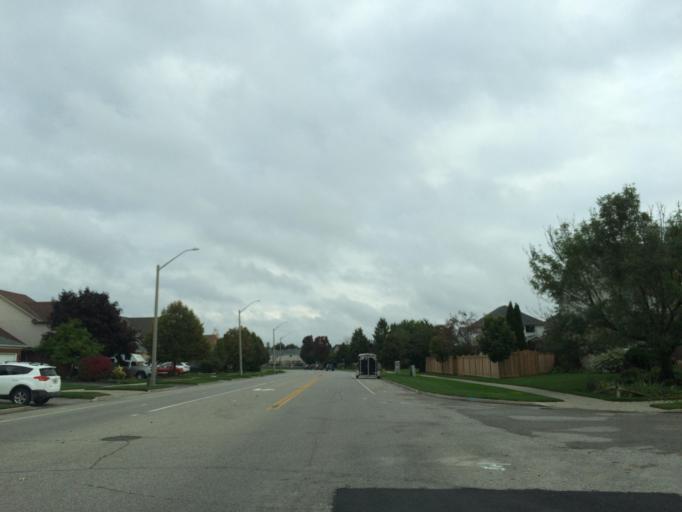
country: CA
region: Ontario
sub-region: Wellington County
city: Guelph
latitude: 43.5682
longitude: -80.2293
